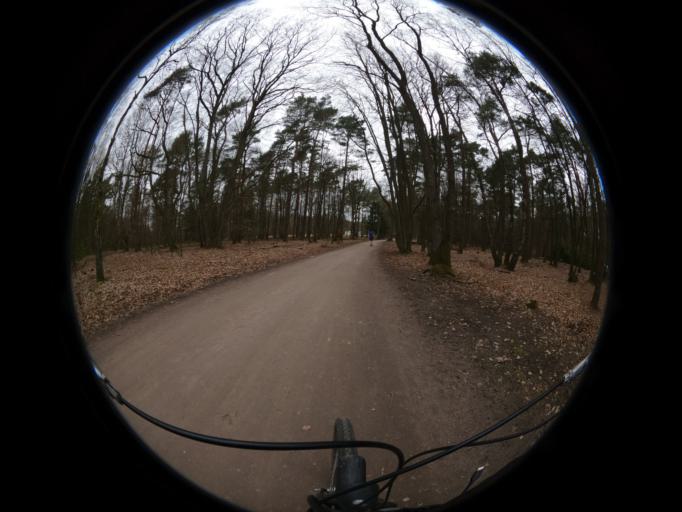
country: DE
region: Lower Saxony
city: Neu Wulmstorf
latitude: 53.4503
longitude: 9.8502
